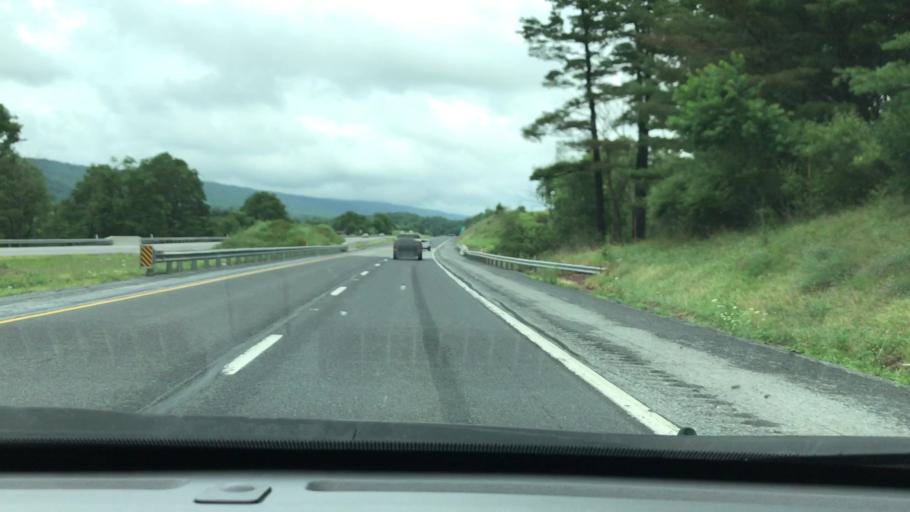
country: US
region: Pennsylvania
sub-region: Bedford County
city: Earlston
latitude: 39.9294
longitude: -78.2324
